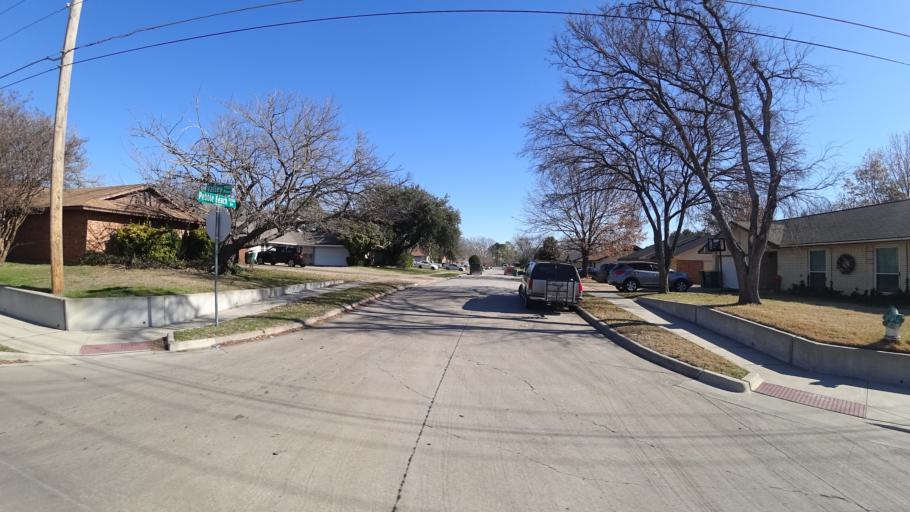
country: US
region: Texas
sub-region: Denton County
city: Lewisville
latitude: 33.0329
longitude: -97.0189
